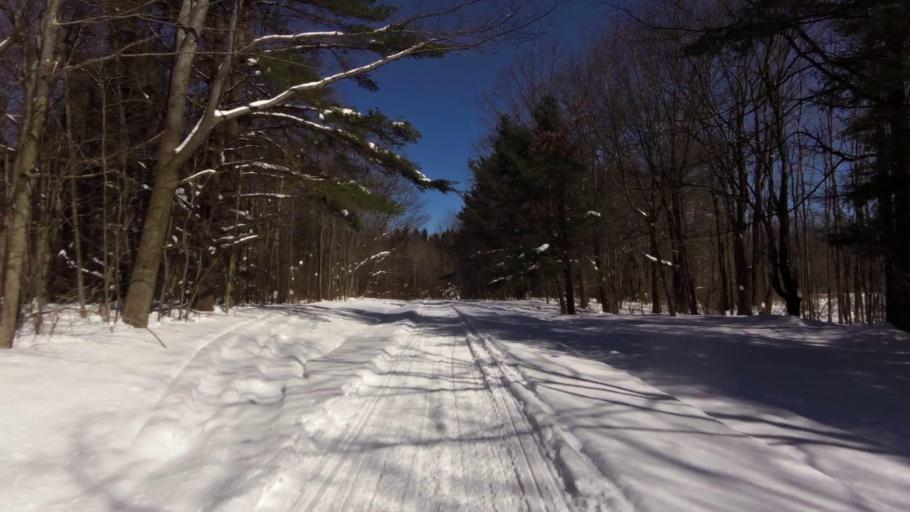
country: US
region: New York
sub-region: Allegany County
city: Cuba
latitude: 42.3256
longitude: -78.2340
